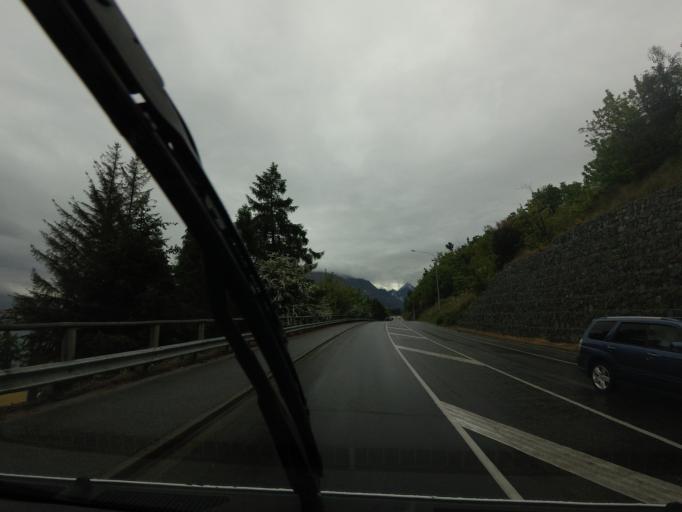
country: NZ
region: Otago
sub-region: Queenstown-Lakes District
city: Queenstown
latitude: -45.0300
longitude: 168.6856
